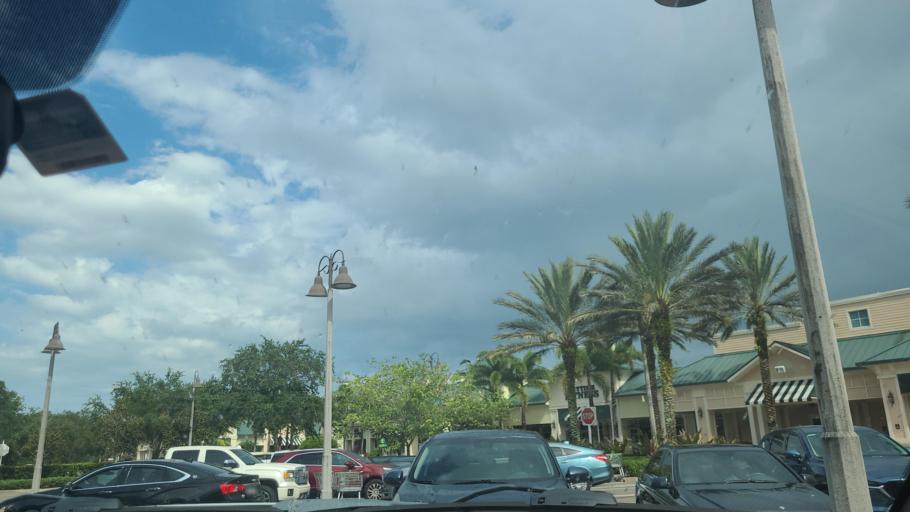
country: US
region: Florida
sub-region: Martin County
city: North River Shores
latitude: 27.2103
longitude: -80.3266
